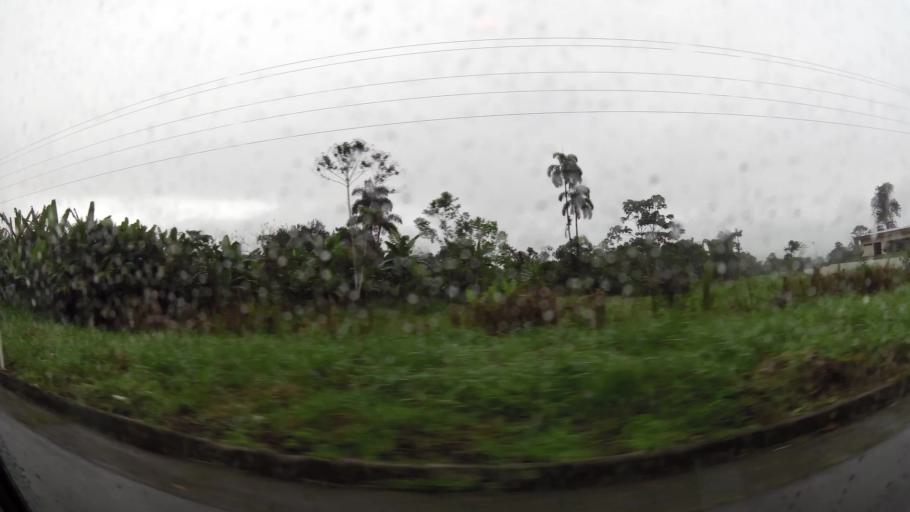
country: EC
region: Santo Domingo de los Tsachilas
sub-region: Canton Santo Domingo de los Colorados
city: Santo Domingo de los Colorados
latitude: -0.2306
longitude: -79.1243
